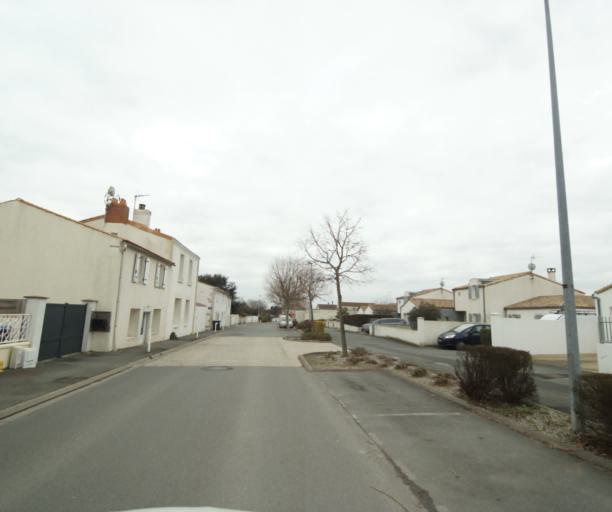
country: FR
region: Poitou-Charentes
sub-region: Departement de la Charente-Maritime
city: Lagord
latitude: 46.1915
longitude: -1.1508
